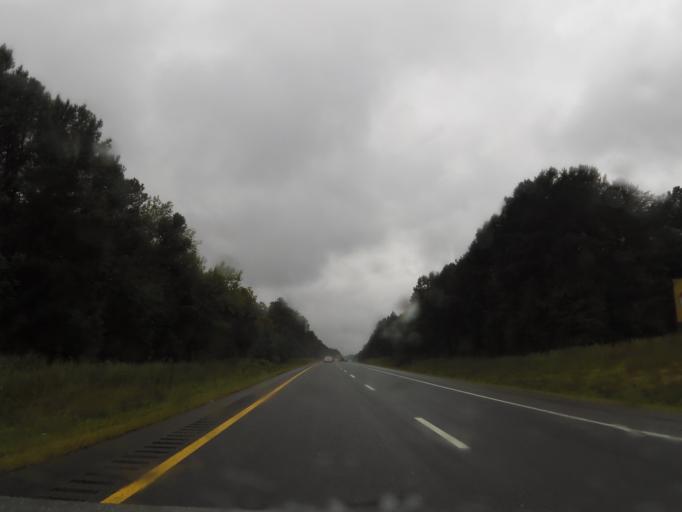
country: US
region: Tennessee
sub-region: Bradley County
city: Hopewell
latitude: 35.2515
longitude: -84.8395
